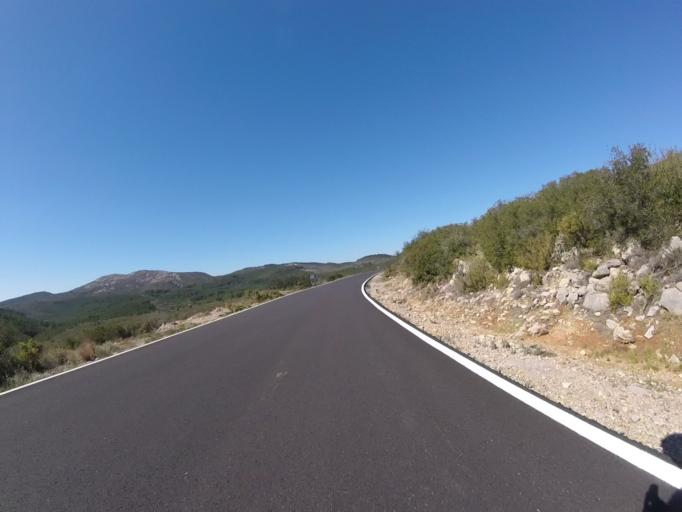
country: ES
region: Valencia
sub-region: Provincia de Castello
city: Cervera del Maestre
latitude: 40.4047
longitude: 0.2123
